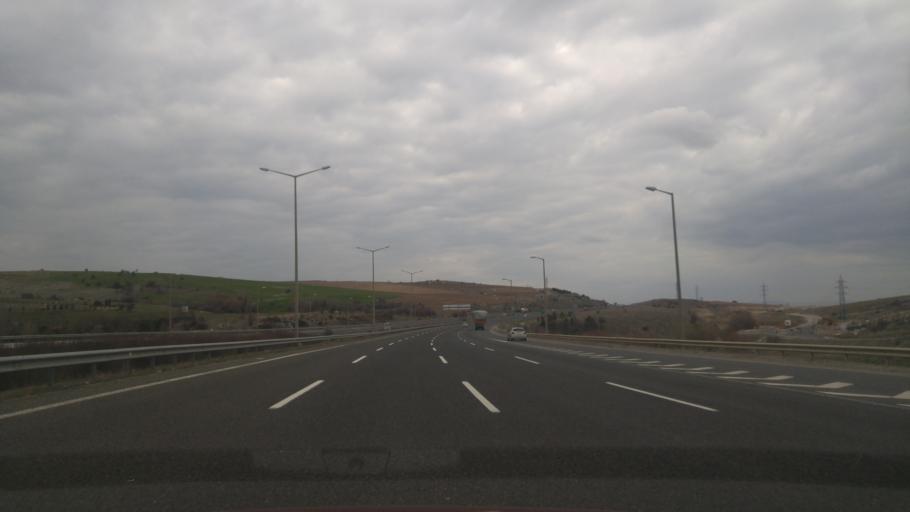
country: TR
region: Ankara
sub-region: Goelbasi
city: Golbasi
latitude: 39.7792
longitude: 32.6698
